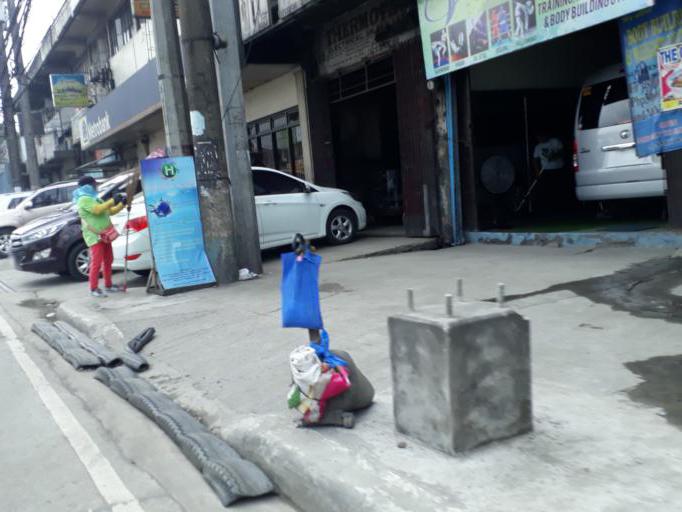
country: PH
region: Calabarzon
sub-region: Province of Rizal
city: Valenzuela
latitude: 14.6871
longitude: 120.9756
